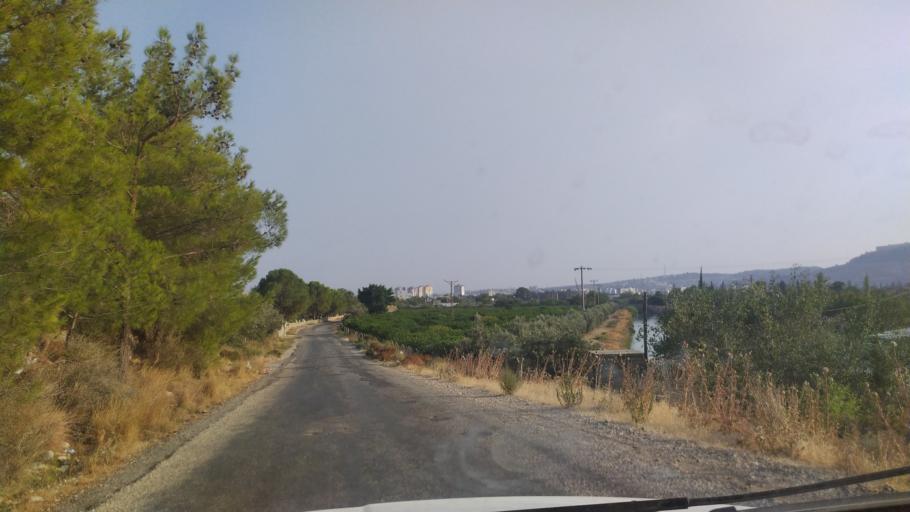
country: TR
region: Mersin
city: Silifke
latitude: 36.4020
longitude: 33.9256
